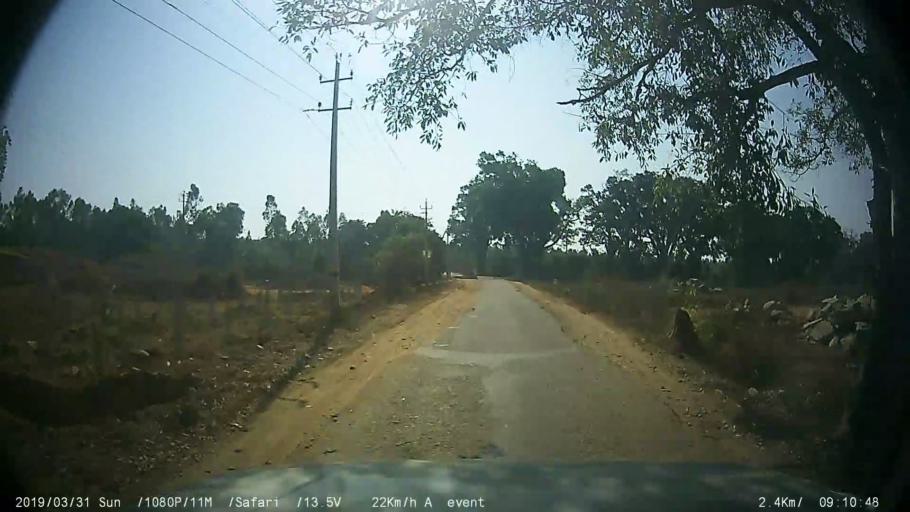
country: IN
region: Karnataka
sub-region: Bangalore Urban
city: Anekal
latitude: 12.8142
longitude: 77.6338
